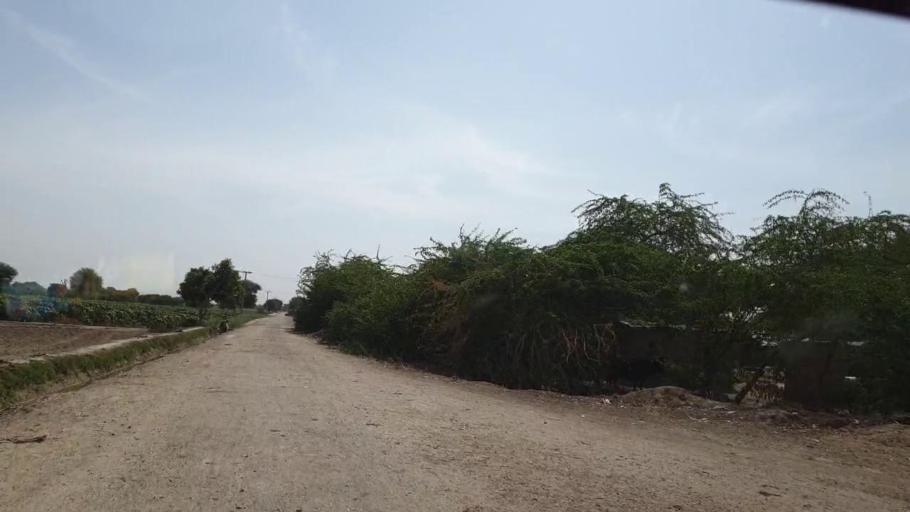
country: PK
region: Sindh
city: Kunri
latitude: 25.1154
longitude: 69.5682
